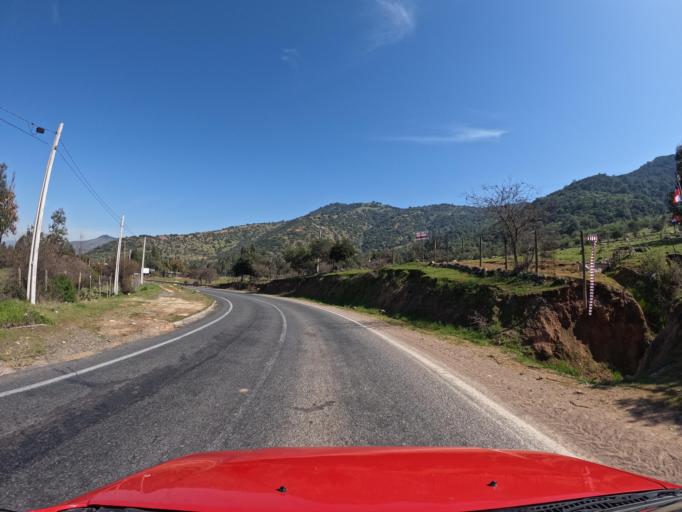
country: CL
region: Maule
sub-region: Provincia de Curico
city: Rauco
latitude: -35.0485
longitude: -71.5972
